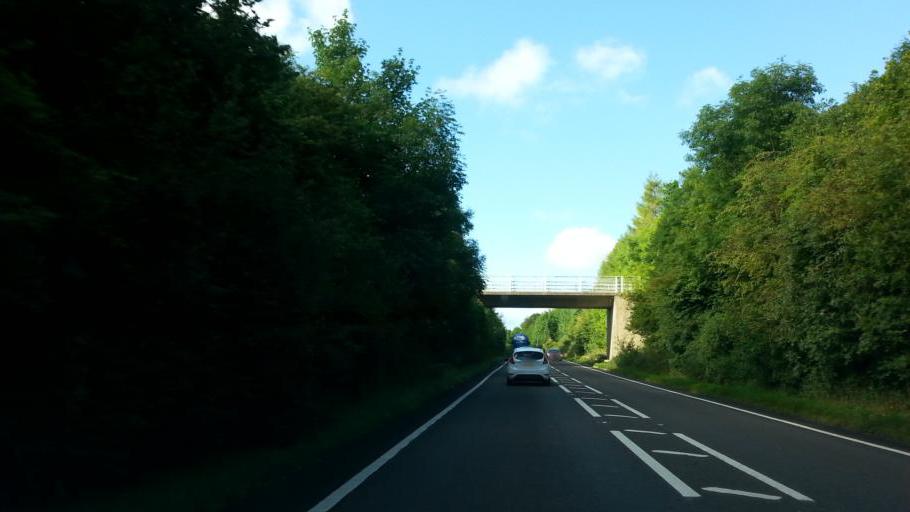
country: GB
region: England
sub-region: District of Rutland
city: South Luffenham
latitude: 52.5401
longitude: -0.5897
